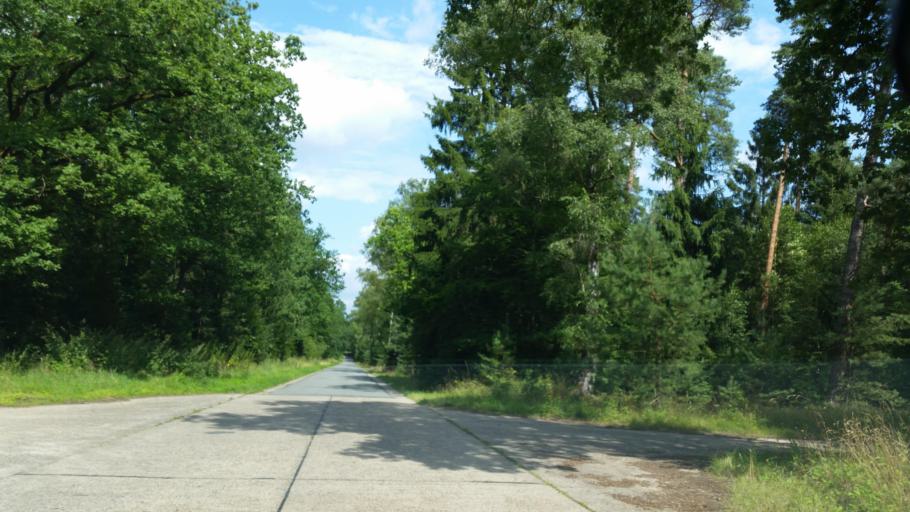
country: DE
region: Lower Saxony
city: Bispingen
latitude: 53.1033
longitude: 9.9089
